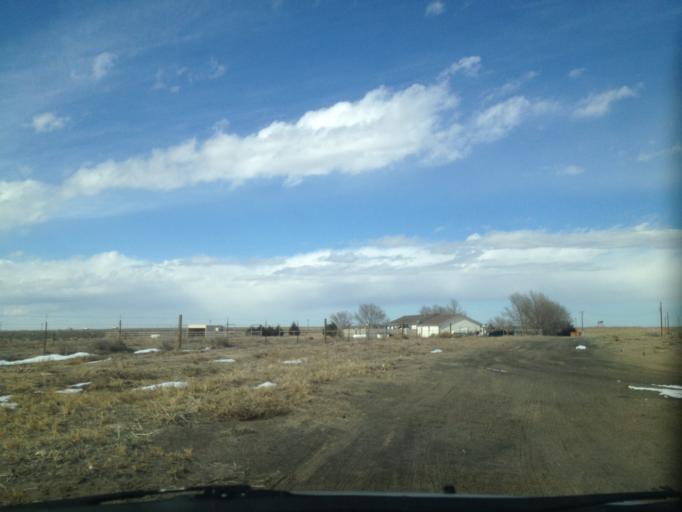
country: US
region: Colorado
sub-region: Weld County
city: Keenesburg
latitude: 40.2875
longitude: -104.2625
